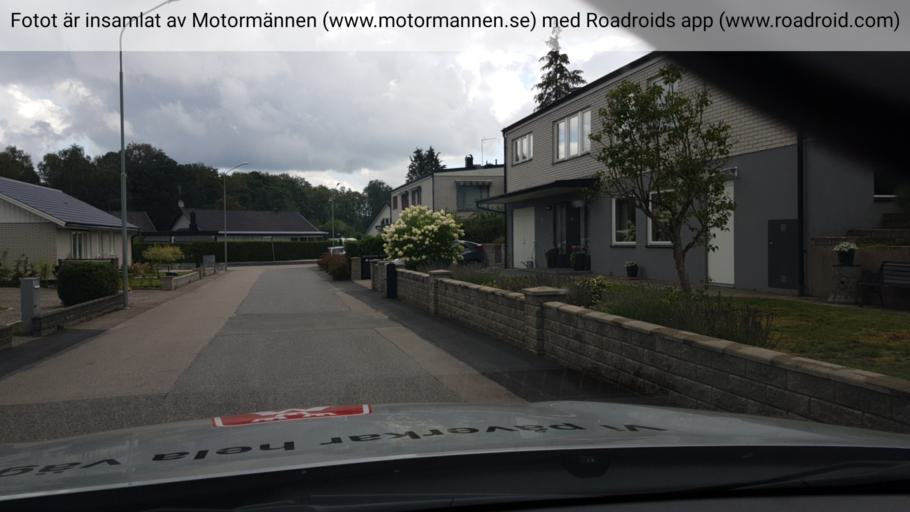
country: SE
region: Skane
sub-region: Hassleholms Kommun
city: Hassleholm
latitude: 56.1547
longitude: 13.7453
